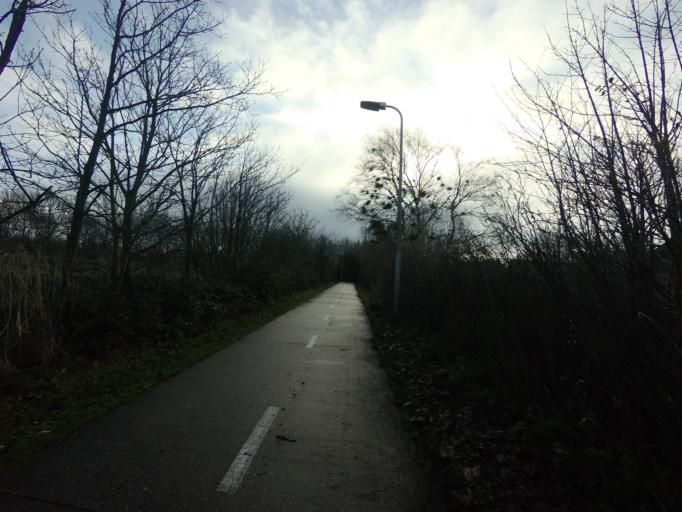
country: NL
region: North Holland
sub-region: Gemeente Texel
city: Den Burg
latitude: 53.1566
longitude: 4.8646
